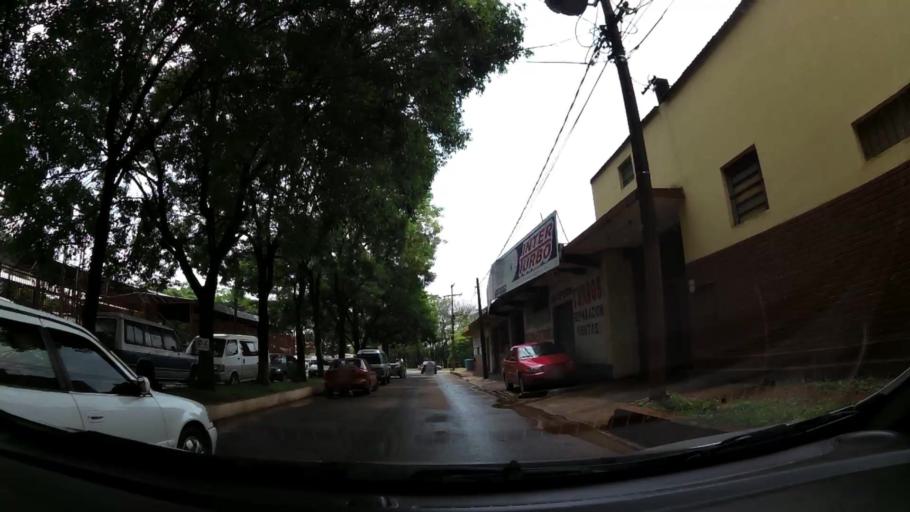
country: PY
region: Alto Parana
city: Ciudad del Este
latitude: -25.5007
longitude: -54.6608
